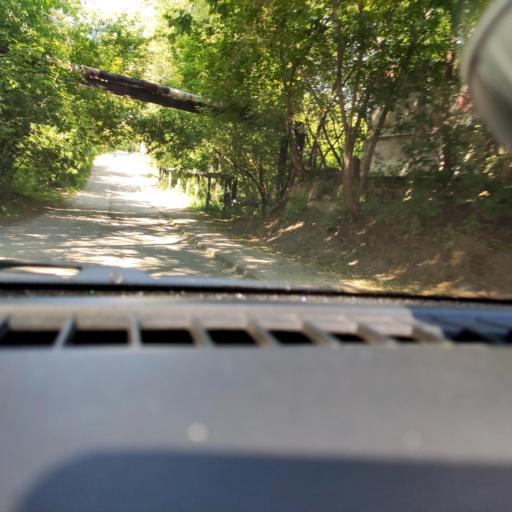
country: RU
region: Perm
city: Polazna
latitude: 58.1233
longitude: 56.3826
